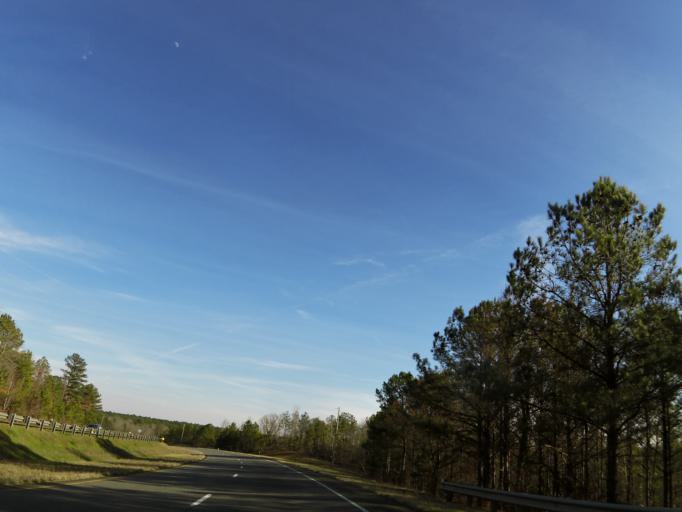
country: US
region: Georgia
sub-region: Stewart County
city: Richland
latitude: 32.1523
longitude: -84.6949
